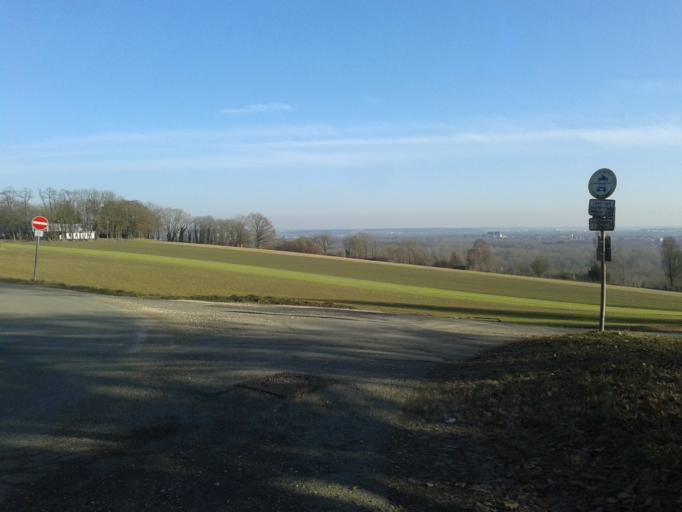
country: DE
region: Baden-Wuerttemberg
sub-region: Tuebingen Region
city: Ulm
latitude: 48.3804
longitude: 9.9542
